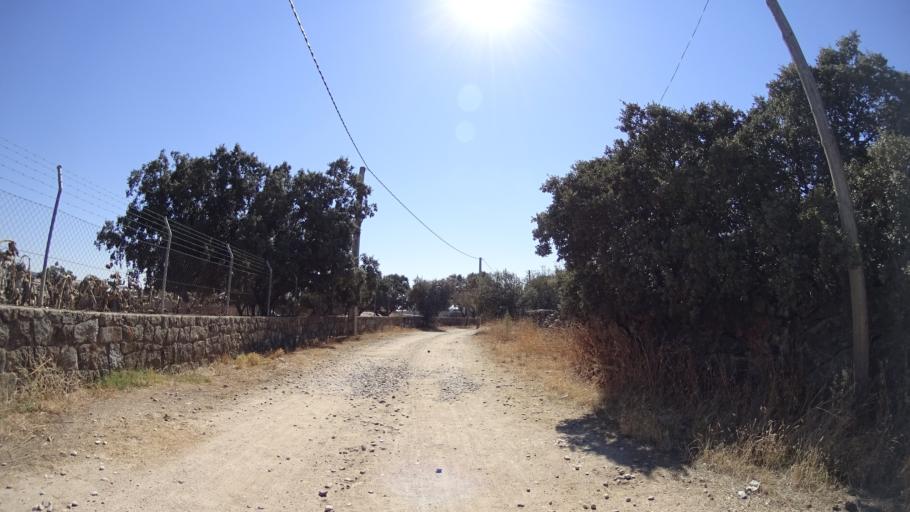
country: ES
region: Madrid
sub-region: Provincia de Madrid
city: Collado-Villalba
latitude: 40.6132
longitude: -4.0038
